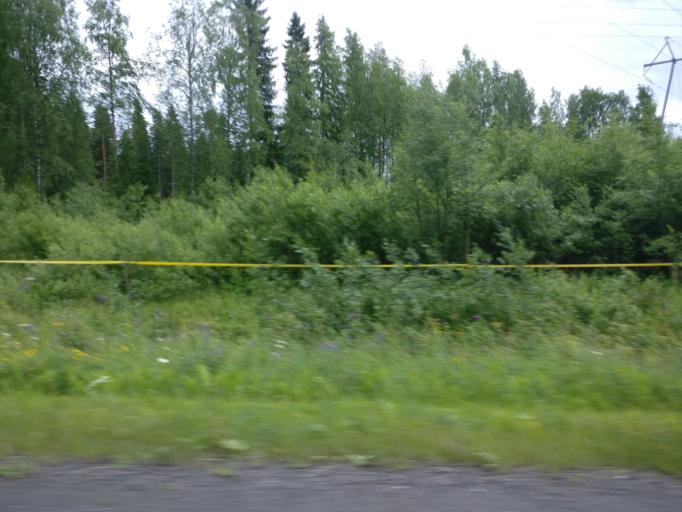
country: FI
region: Northern Savo
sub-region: Varkaus
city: Varkaus
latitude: 62.3975
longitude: 27.8208
